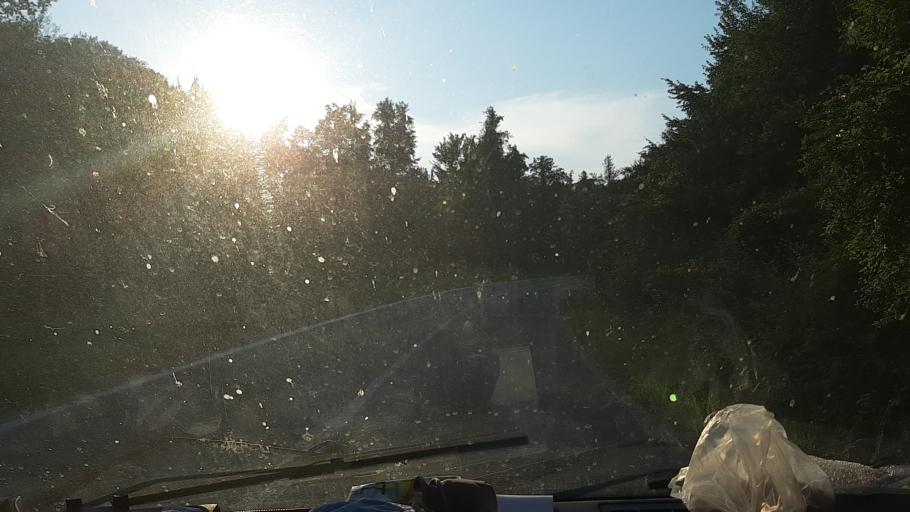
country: RO
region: Caras-Severin
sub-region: Municipiul Resita
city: Calnic
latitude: 45.3433
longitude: 21.8353
